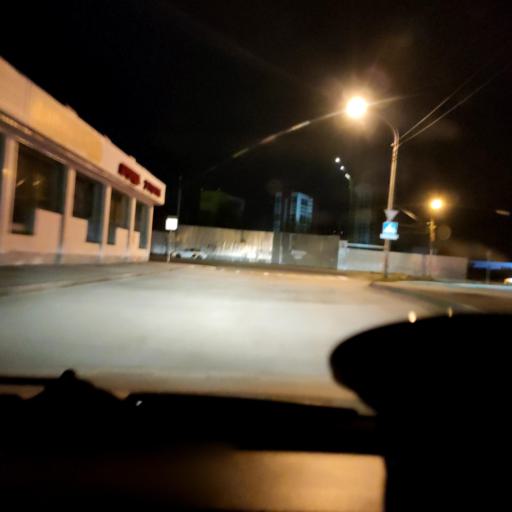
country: RU
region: Perm
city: Perm
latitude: 57.9721
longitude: 56.2314
